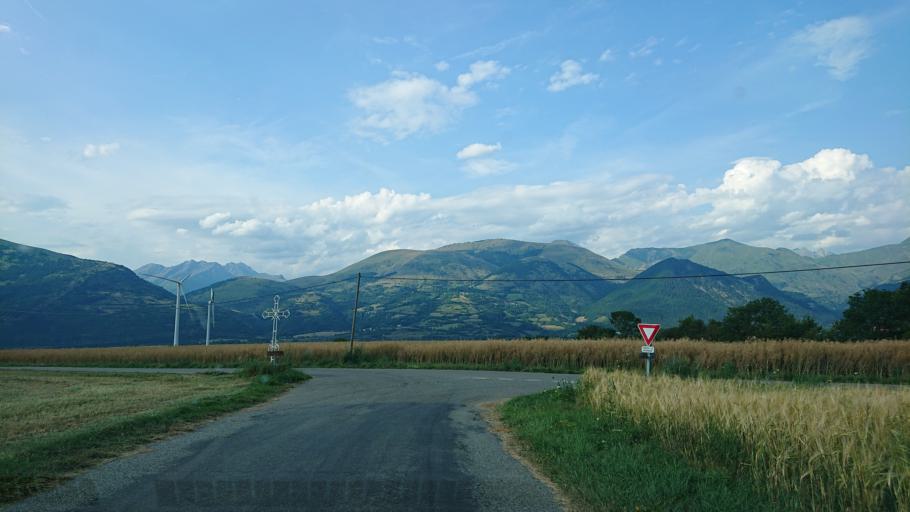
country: FR
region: Rhone-Alpes
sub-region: Departement de l'Isere
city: Mens
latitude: 44.8012
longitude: 5.9065
